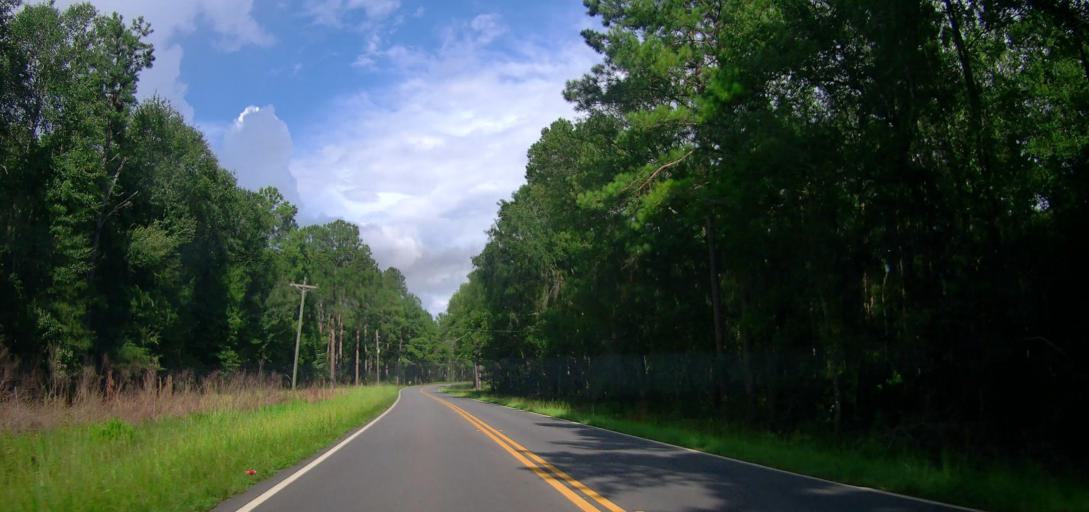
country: US
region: Georgia
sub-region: Coffee County
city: Douglas
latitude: 31.4516
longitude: -82.8837
